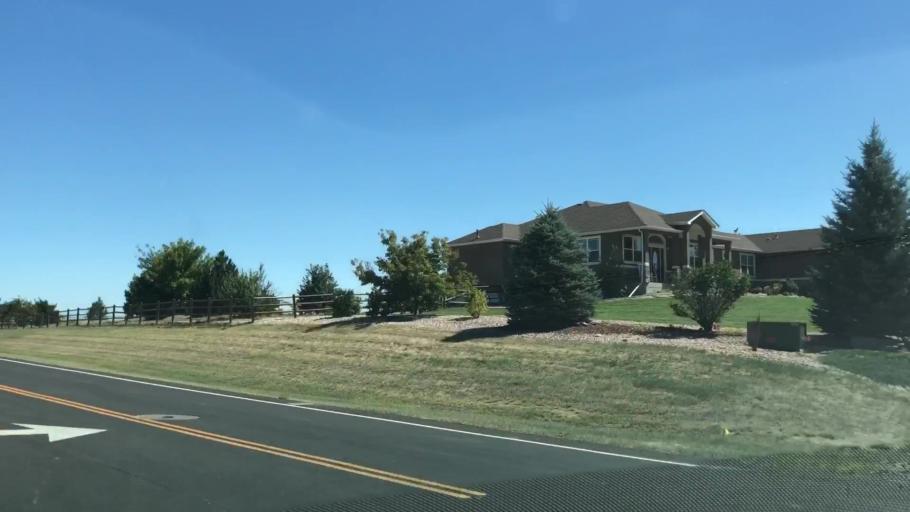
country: US
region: Colorado
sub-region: Weld County
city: Windsor
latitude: 40.4457
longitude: -104.9463
